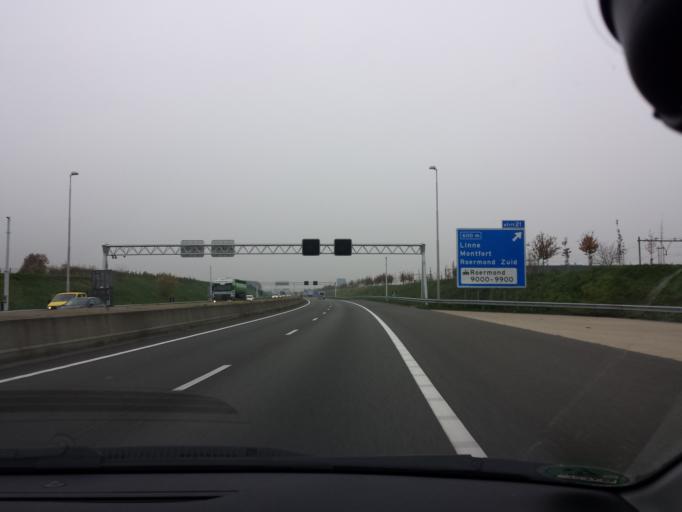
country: NL
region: Limburg
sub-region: Gemeente Roermond
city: Roermond
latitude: 51.1732
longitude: 5.9796
